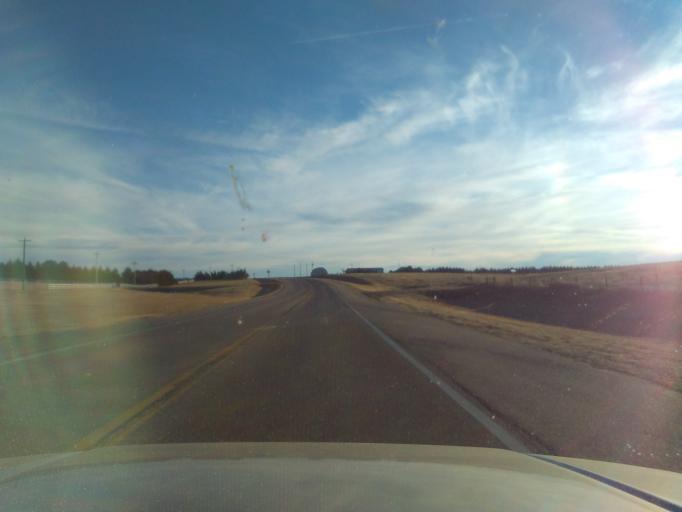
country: US
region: Kansas
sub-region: Logan County
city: Oakley
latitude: 39.1816
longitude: -100.8701
